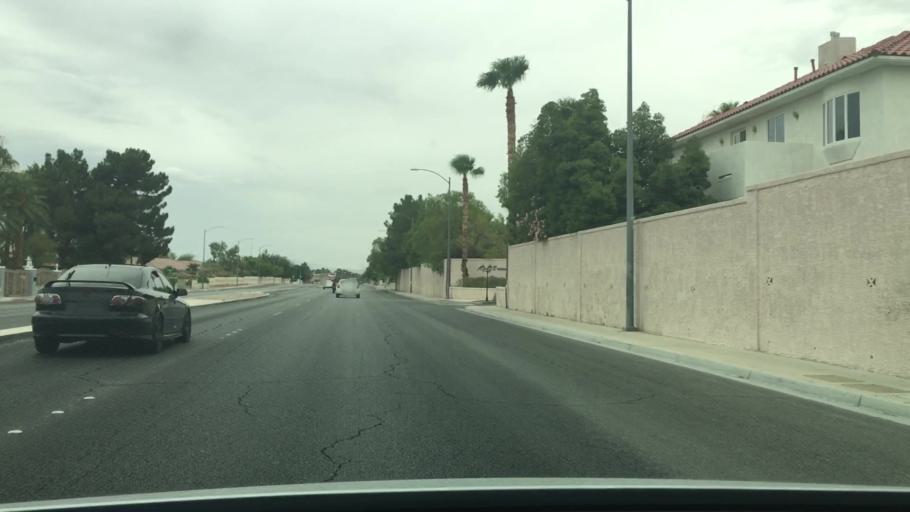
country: US
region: Nevada
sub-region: Clark County
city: Spring Valley
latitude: 36.1489
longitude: -115.2615
